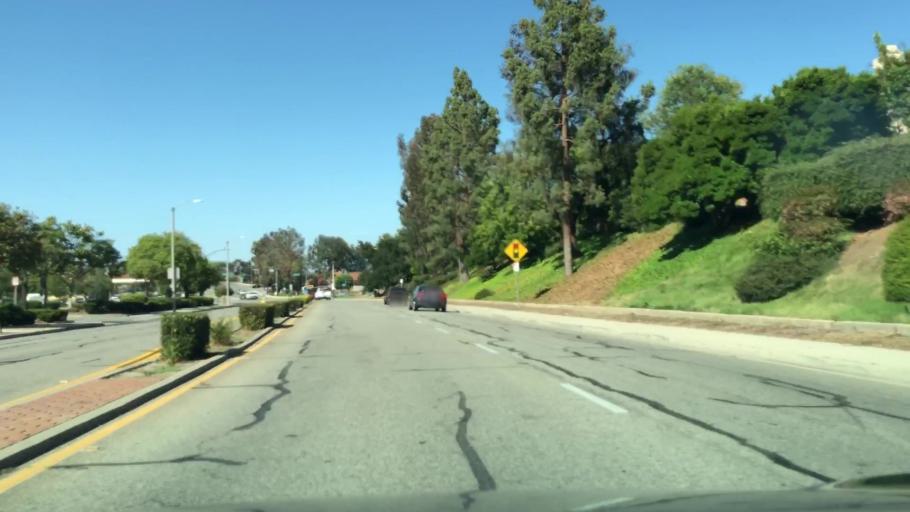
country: US
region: California
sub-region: Ventura County
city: Casa Conejo
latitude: 34.1808
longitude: -118.9288
